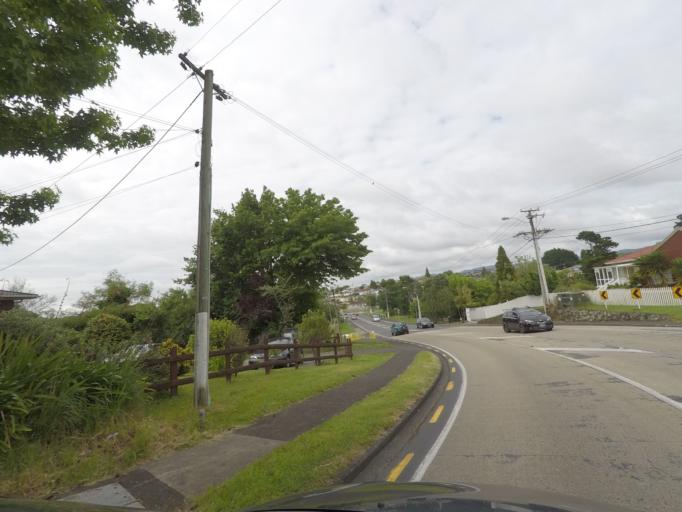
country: NZ
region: Auckland
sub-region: Auckland
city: Rosebank
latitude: -36.8573
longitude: 174.6097
